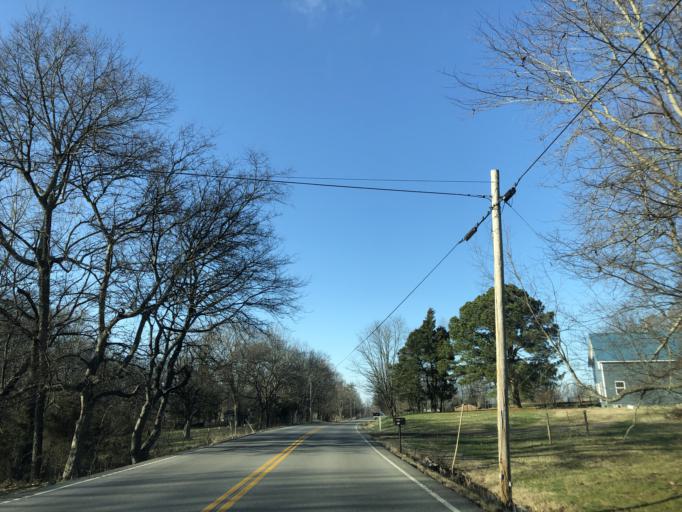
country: US
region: Tennessee
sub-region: Sumner County
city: White House
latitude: 36.5026
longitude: -86.6070
